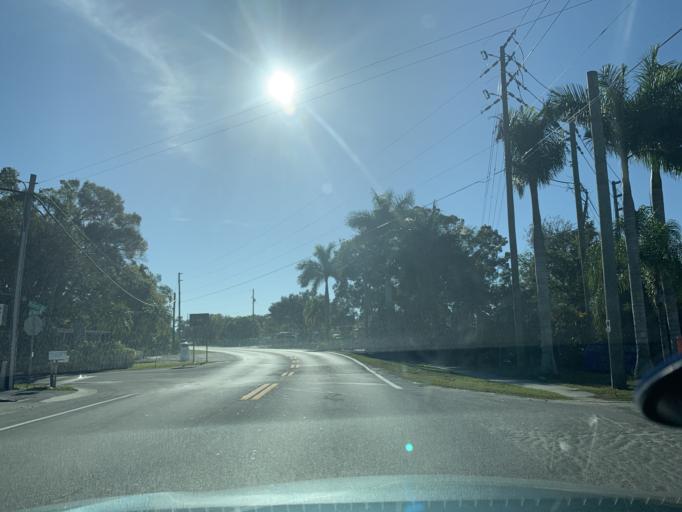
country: US
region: Florida
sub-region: Pinellas County
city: Lealman
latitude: 27.8276
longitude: -82.6755
